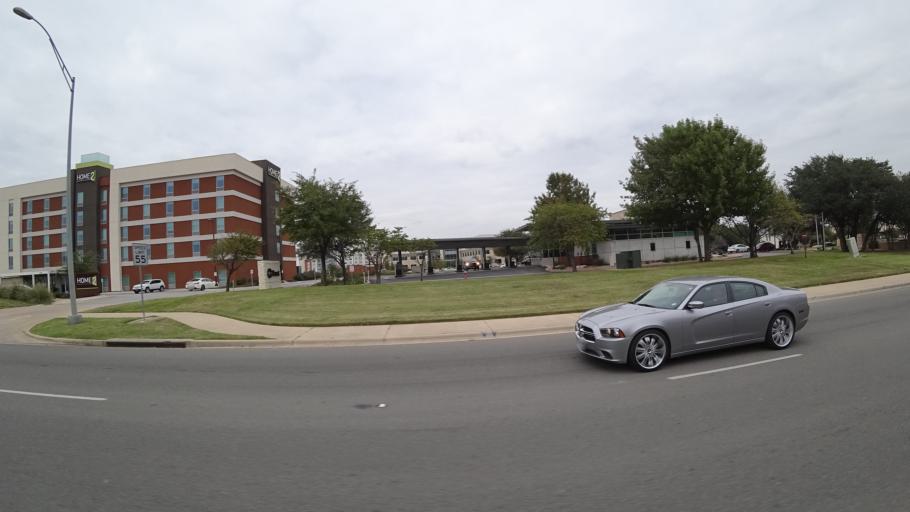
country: US
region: Texas
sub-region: Williamson County
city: Round Rock
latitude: 30.4796
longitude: -97.6858
